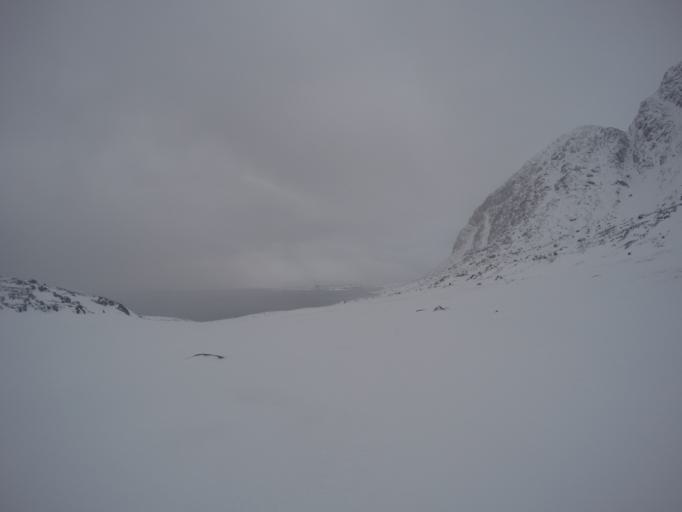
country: GL
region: Sermersooq
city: Nuuk
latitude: 64.1423
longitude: -51.6683
